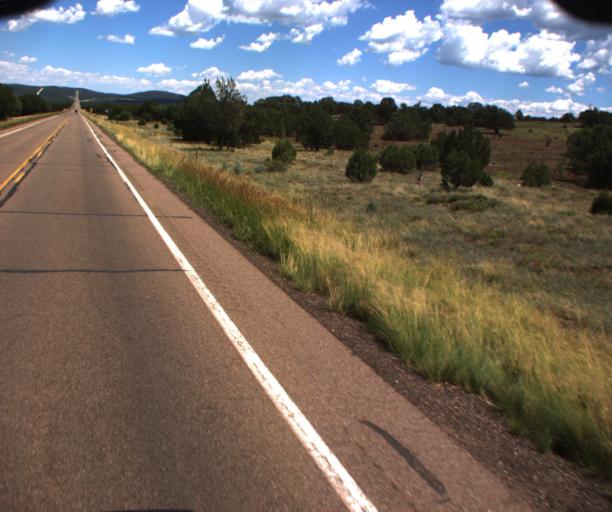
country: US
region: Arizona
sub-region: Navajo County
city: White Mountain Lake
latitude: 34.2777
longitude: -109.8841
